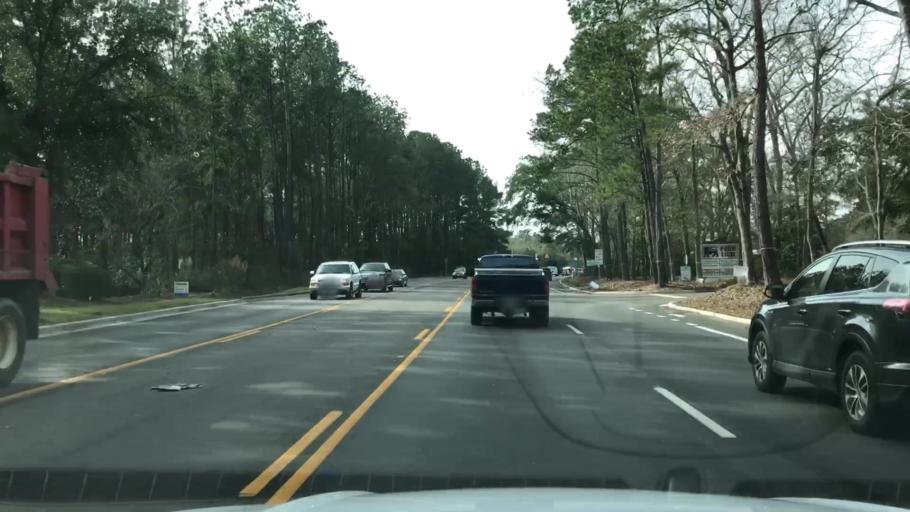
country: US
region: South Carolina
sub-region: Charleston County
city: Shell Point
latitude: 32.7451
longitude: -80.0365
